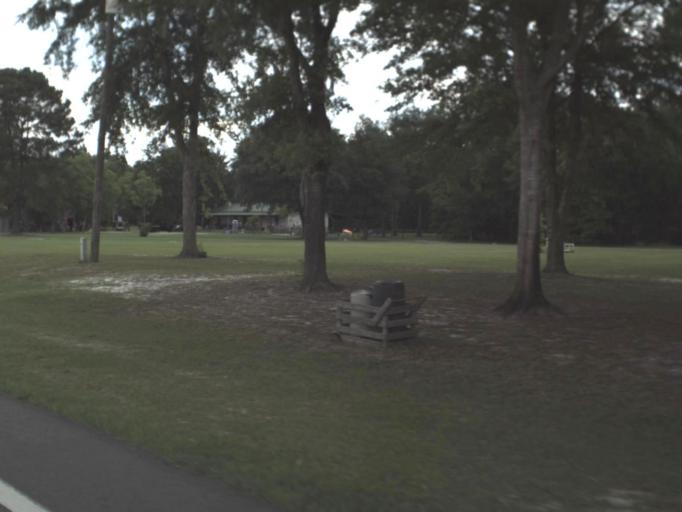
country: US
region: Florida
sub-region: Columbia County
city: Five Points
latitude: 30.3634
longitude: -82.6194
